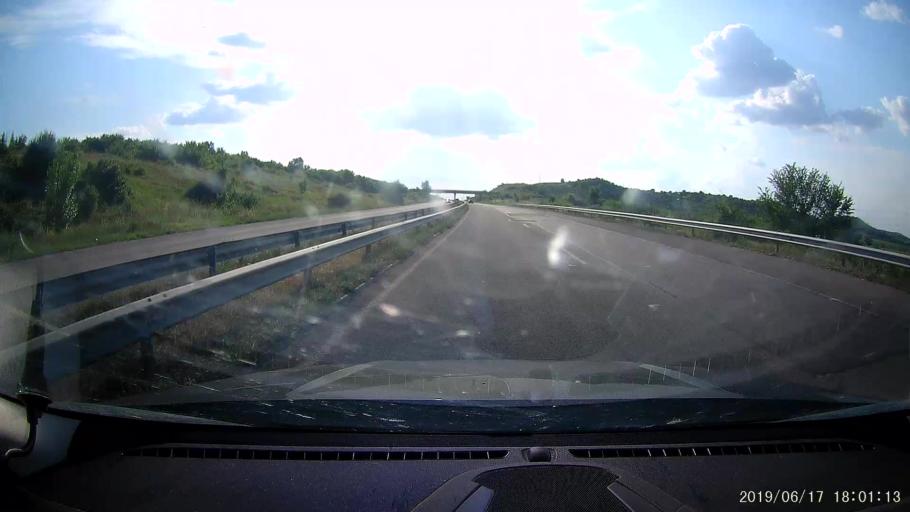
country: BG
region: Khaskovo
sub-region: Obshtina Svilengrad
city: Svilengrad
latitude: 41.7448
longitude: 26.2610
